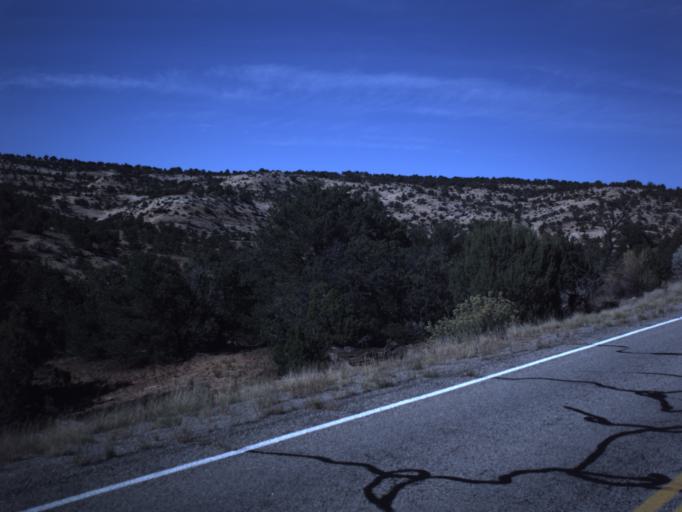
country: US
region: Utah
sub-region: San Juan County
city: Monticello
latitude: 37.9898
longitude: -109.4942
